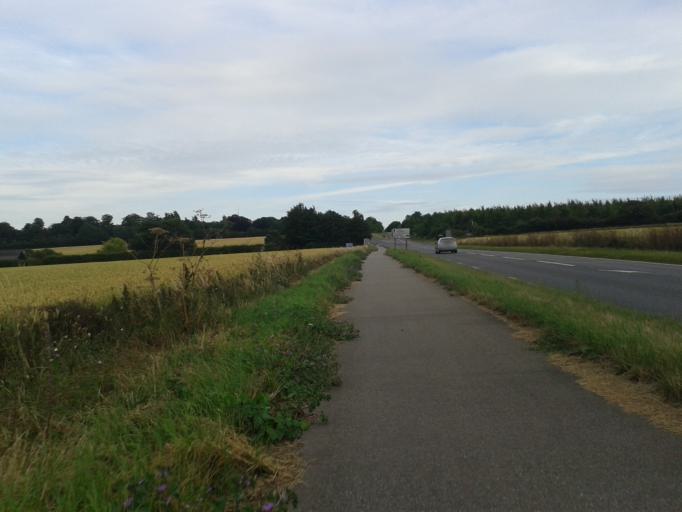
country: GB
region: England
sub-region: Cambridgeshire
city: Sawston
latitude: 52.1609
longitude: 0.1718
